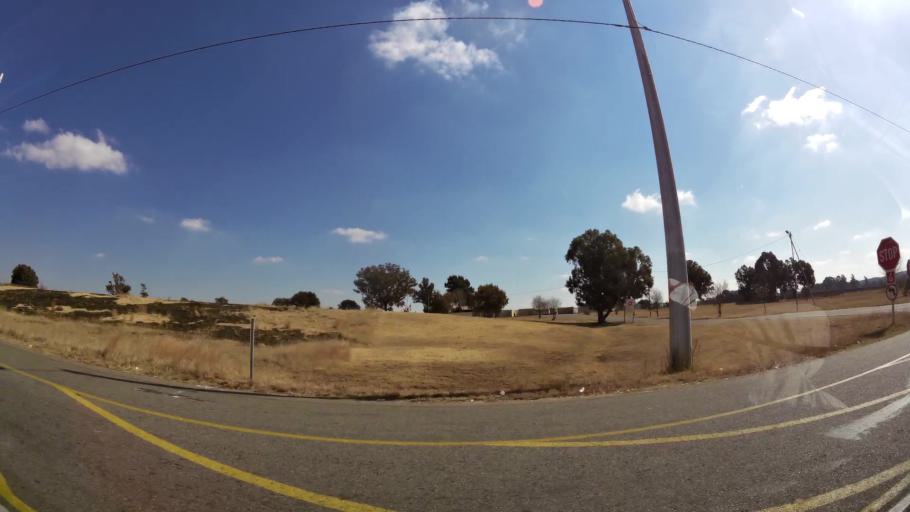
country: ZA
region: Gauteng
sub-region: West Rand District Municipality
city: Randfontein
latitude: -26.1563
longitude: 27.7624
